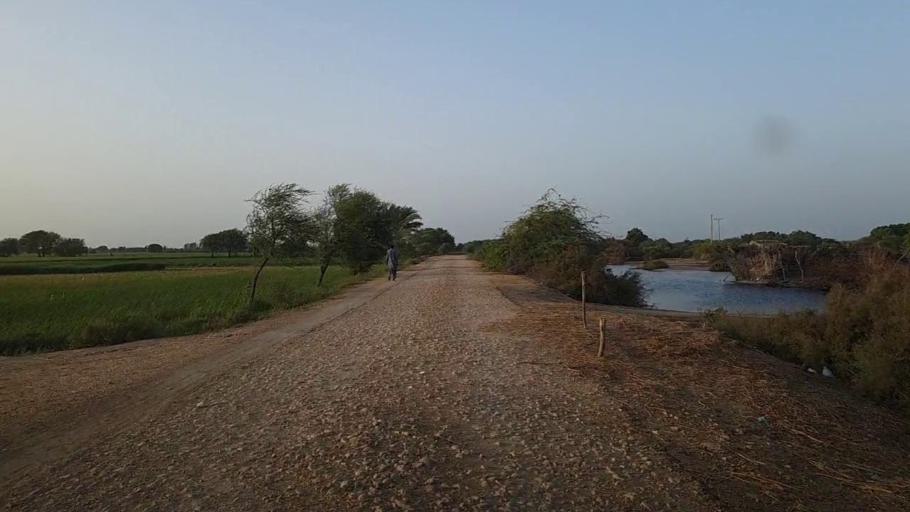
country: PK
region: Sindh
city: Kario
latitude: 24.7170
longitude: 68.4621
